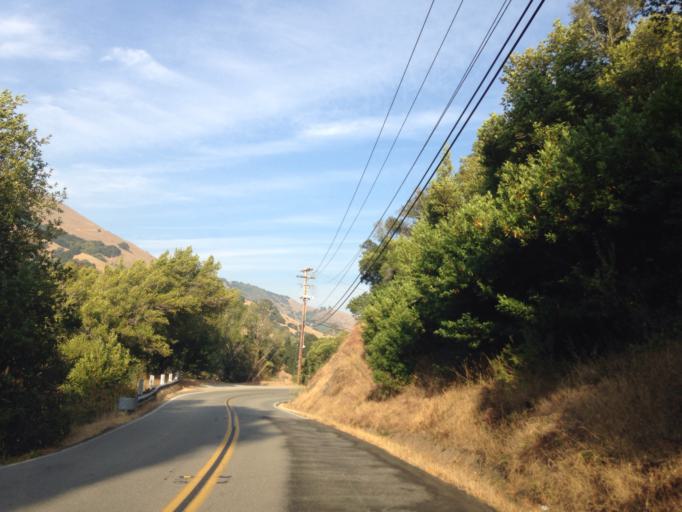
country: US
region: California
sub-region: Marin County
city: Lucas Valley-Marinwood
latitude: 38.0385
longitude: -122.6027
